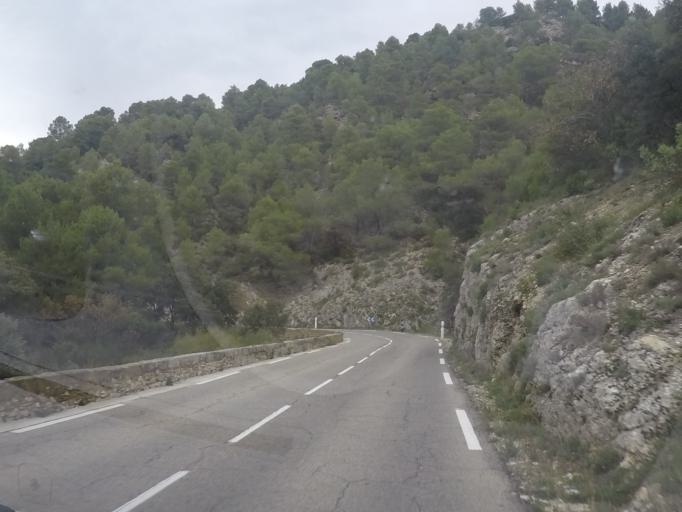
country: FR
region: Provence-Alpes-Cote d'Azur
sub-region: Departement du Vaucluse
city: Lourmarin
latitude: 43.7797
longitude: 5.3494
